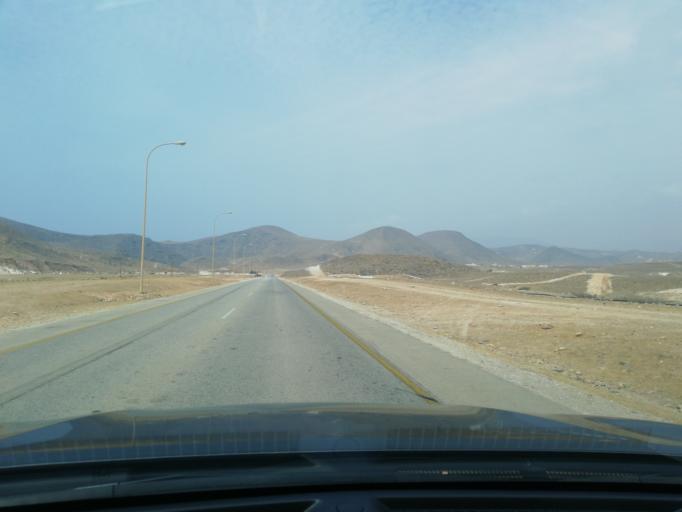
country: OM
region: Zufar
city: Salalah
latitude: 16.9097
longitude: 53.8281
